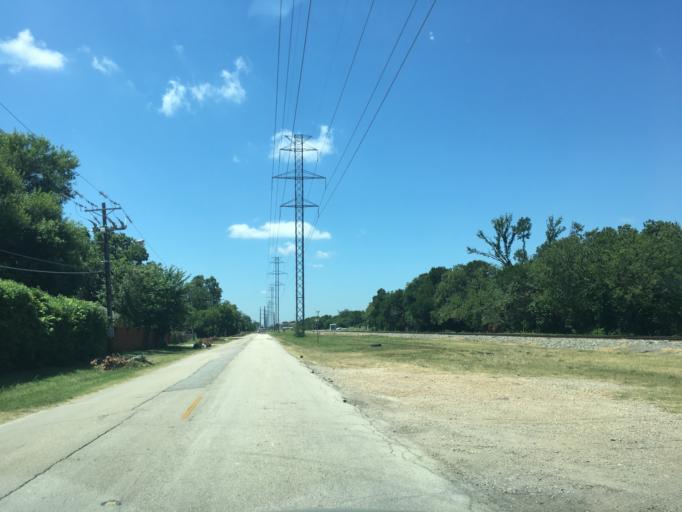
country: US
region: Texas
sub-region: Dallas County
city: Garland
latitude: 32.8425
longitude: -96.6851
